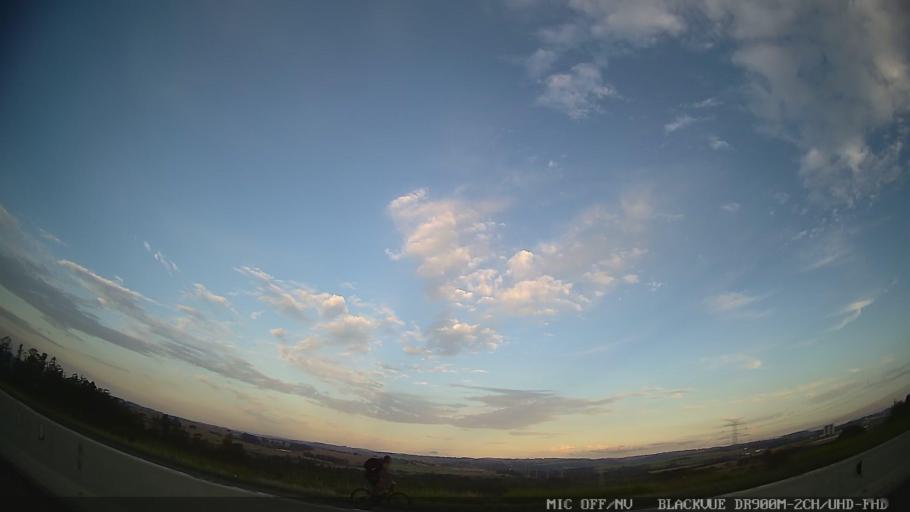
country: BR
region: Sao Paulo
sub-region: Salto
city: Salto
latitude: -23.1616
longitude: -47.2637
